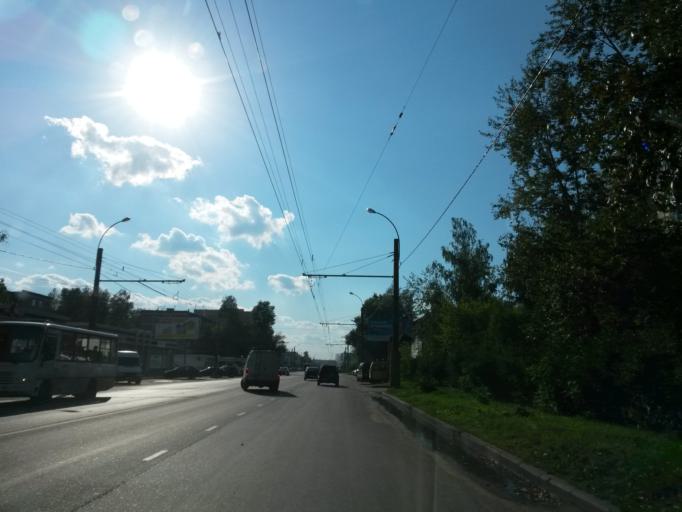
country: RU
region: Ivanovo
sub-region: Gorod Ivanovo
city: Ivanovo
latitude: 56.9577
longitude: 40.9889
